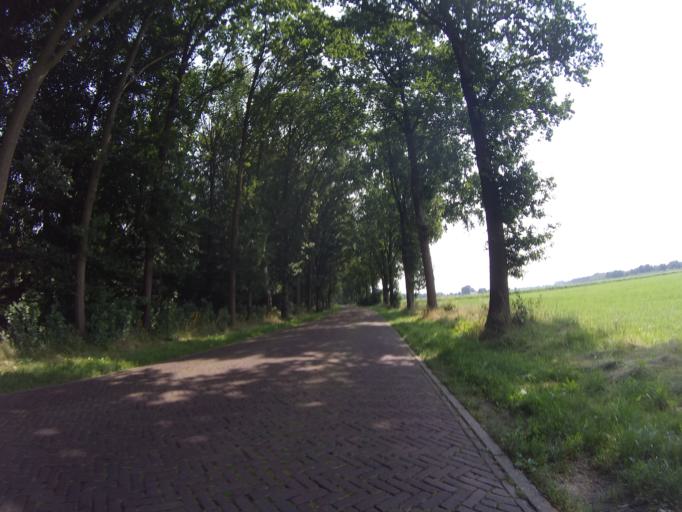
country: NL
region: Drenthe
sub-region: Gemeente Coevorden
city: Sleen
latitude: 52.7976
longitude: 6.6951
